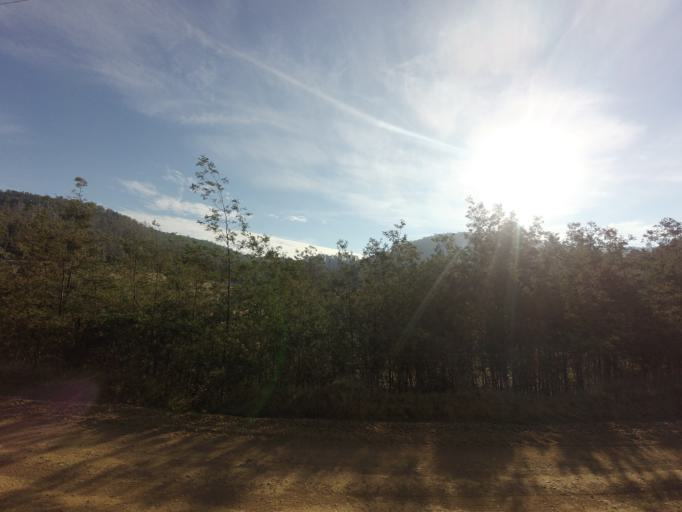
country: AU
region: Tasmania
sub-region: Sorell
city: Sorell
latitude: -42.4898
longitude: 147.4331
